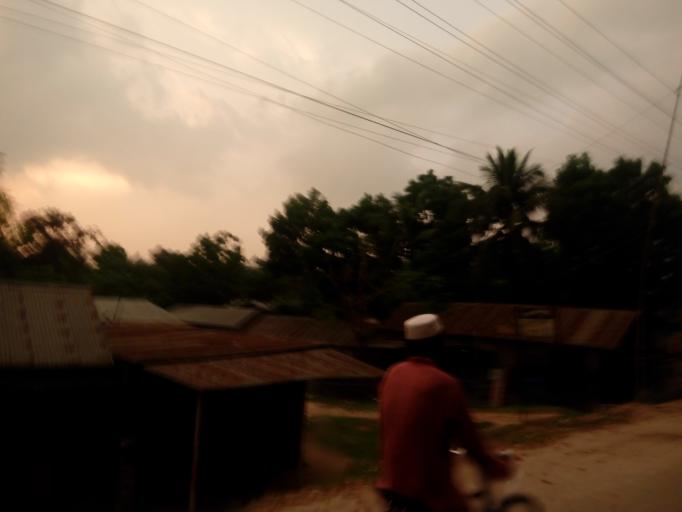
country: BD
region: Rajshahi
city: Sirajganj
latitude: 24.3023
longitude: 89.6975
